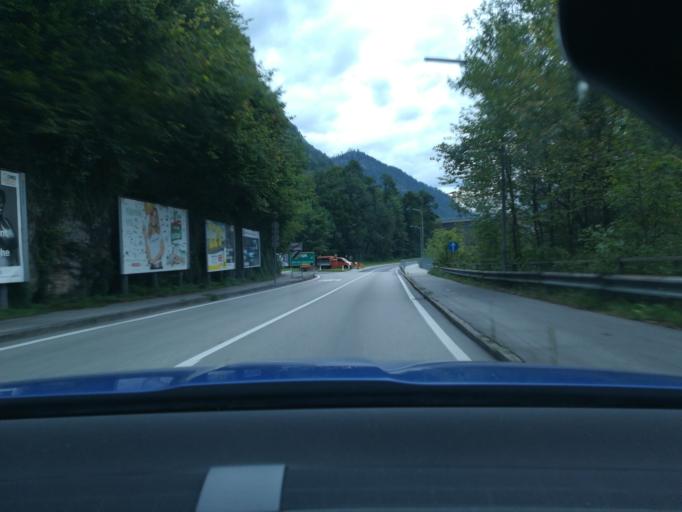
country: AT
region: Upper Austria
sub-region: Politischer Bezirk Gmunden
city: Bad Ischl
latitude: 47.7151
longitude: 13.6267
